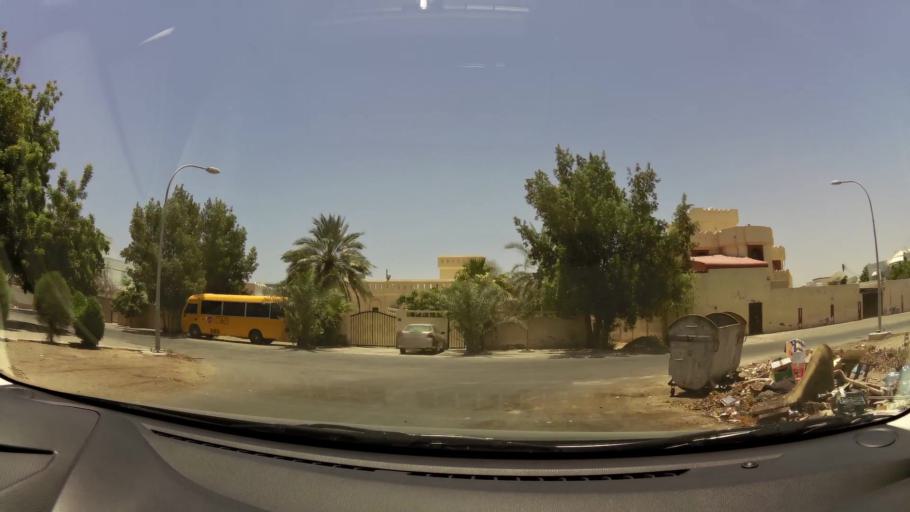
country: OM
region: Muhafazat Masqat
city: As Sib al Jadidah
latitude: 23.6349
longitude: 58.2333
